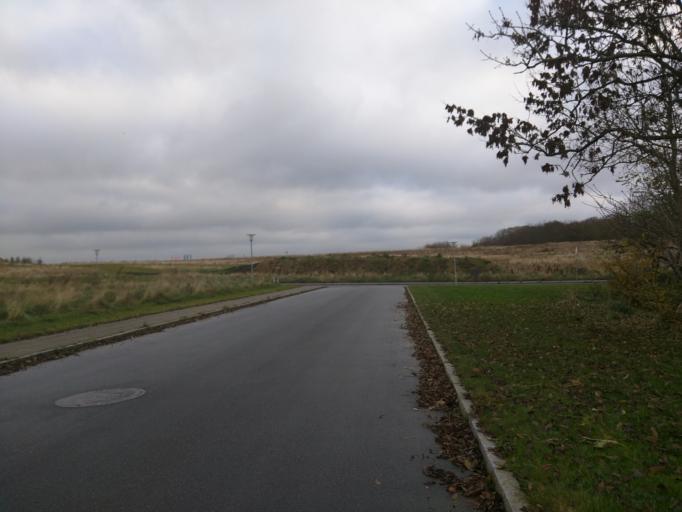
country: DK
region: Central Jutland
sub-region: Viborg Kommune
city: Viborg
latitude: 56.4418
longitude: 9.3646
